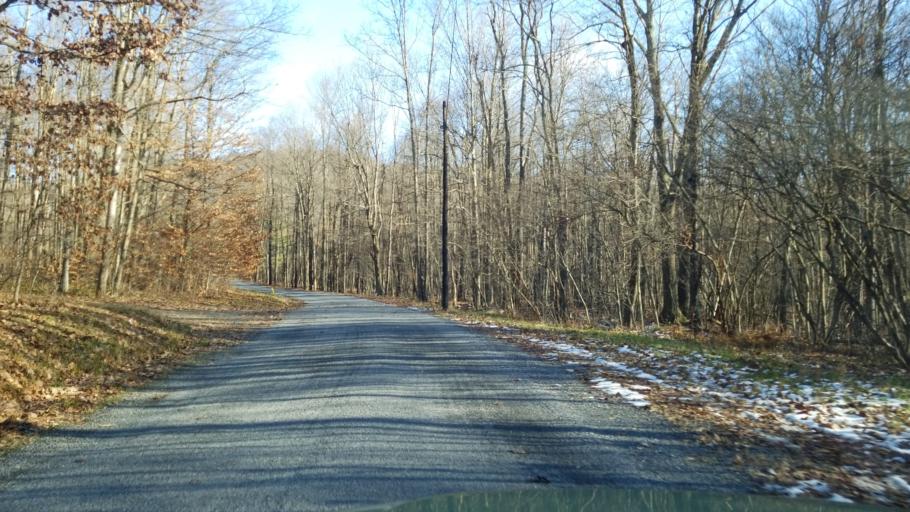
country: US
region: Pennsylvania
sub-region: Jefferson County
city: Brockway
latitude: 41.2732
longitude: -78.8089
